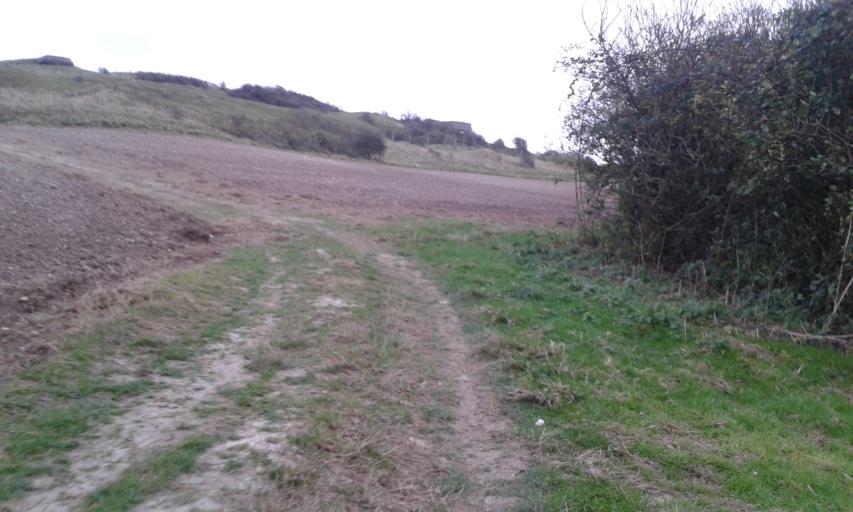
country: FR
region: Nord-Pas-de-Calais
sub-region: Departement du Pas-de-Calais
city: Wissant
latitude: 50.8719
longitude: 1.7018
